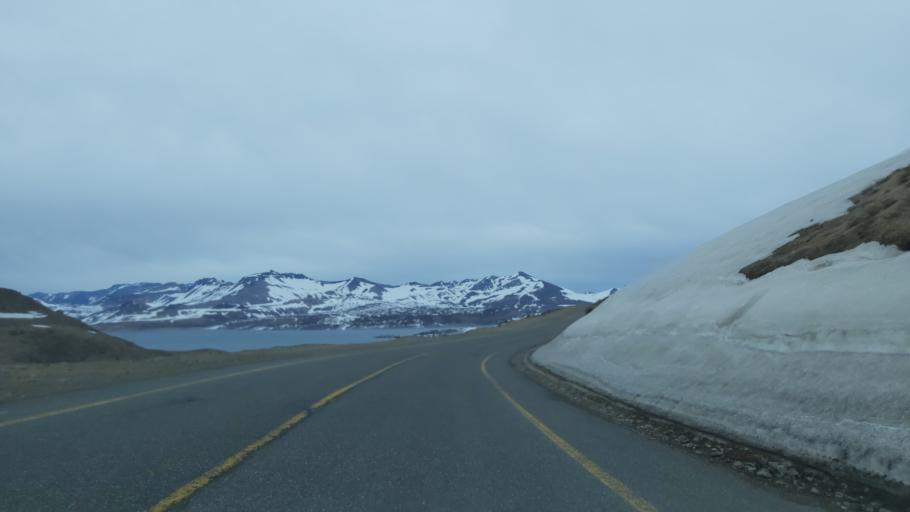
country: CL
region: Maule
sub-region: Provincia de Linares
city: Colbun
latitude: -36.0212
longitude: -70.5005
